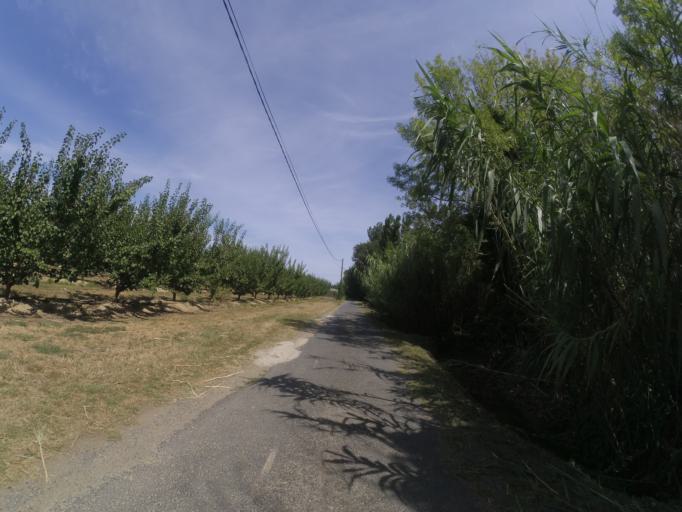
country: FR
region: Languedoc-Roussillon
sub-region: Departement des Pyrenees-Orientales
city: Millas
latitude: 42.6837
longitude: 2.6746
